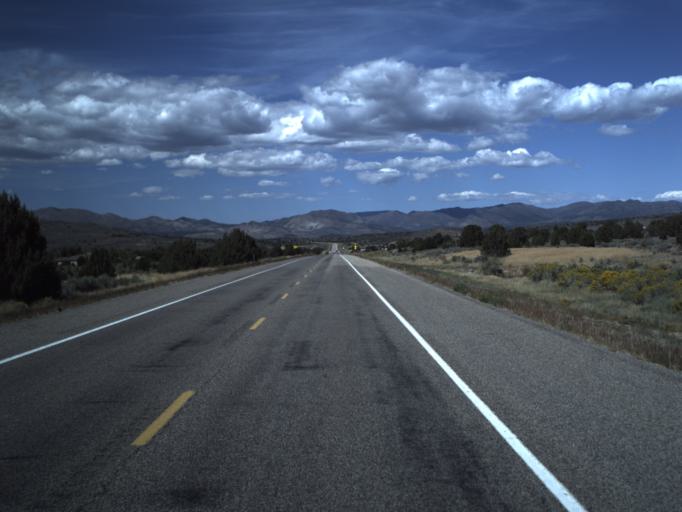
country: US
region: Utah
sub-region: Washington County
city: Ivins
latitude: 37.2952
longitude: -113.6632
